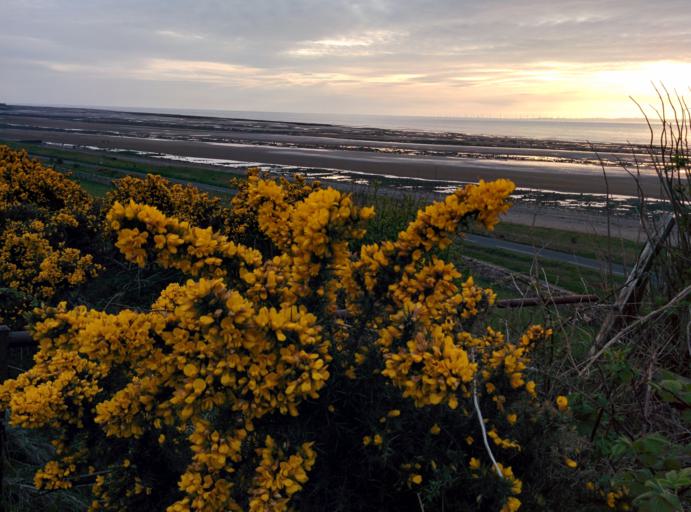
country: GB
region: England
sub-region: Cumbria
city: Dearham
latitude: 54.7465
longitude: -3.4510
